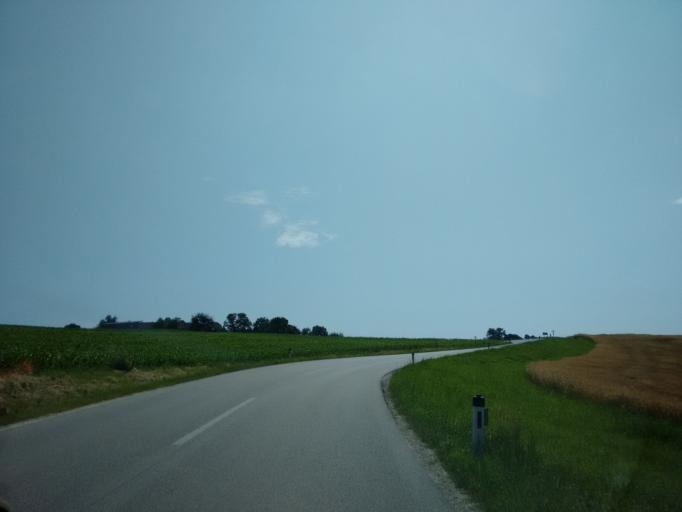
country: AT
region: Upper Austria
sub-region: Politischer Bezirk Urfahr-Umgebung
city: Altenberg bei Linz
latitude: 48.3687
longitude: 14.3317
